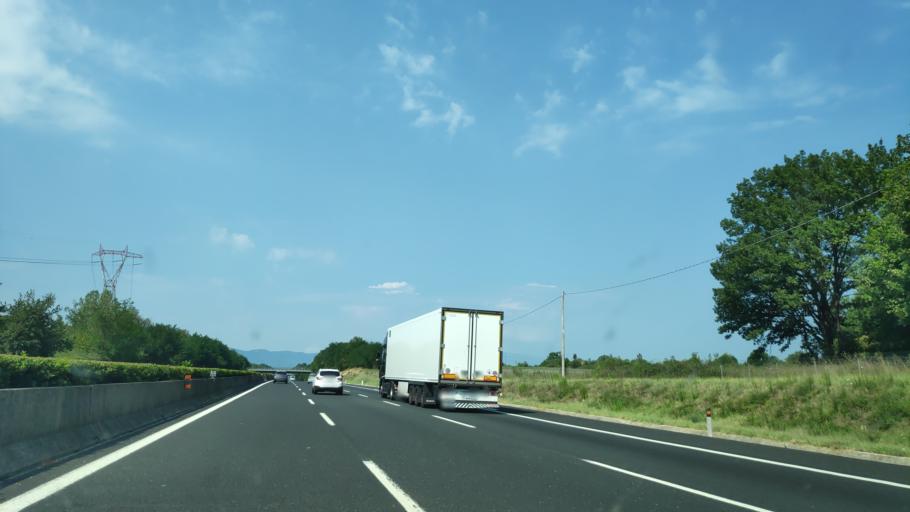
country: IT
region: Latium
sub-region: Provincia di Frosinone
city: Ceprano
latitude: 41.5442
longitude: 13.5545
